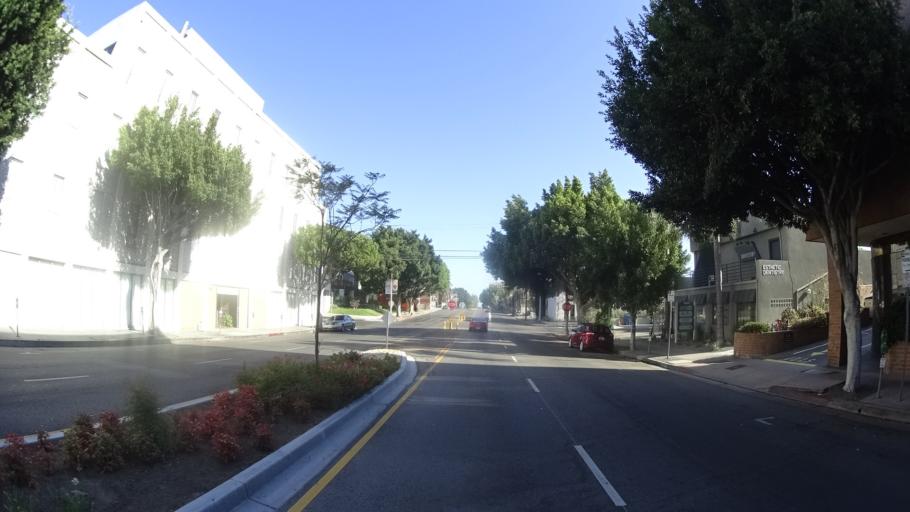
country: US
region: California
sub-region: Los Angeles County
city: Hollywood
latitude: 34.0822
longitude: -118.3237
